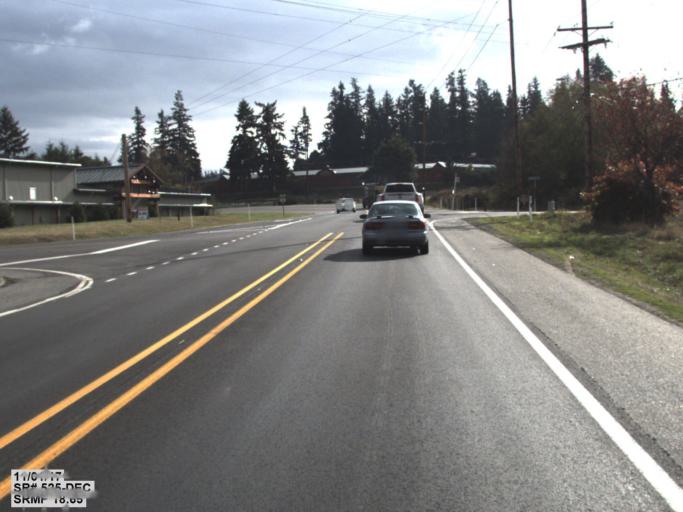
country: US
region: Washington
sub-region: Island County
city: Freeland
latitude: 48.0122
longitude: -122.5418
